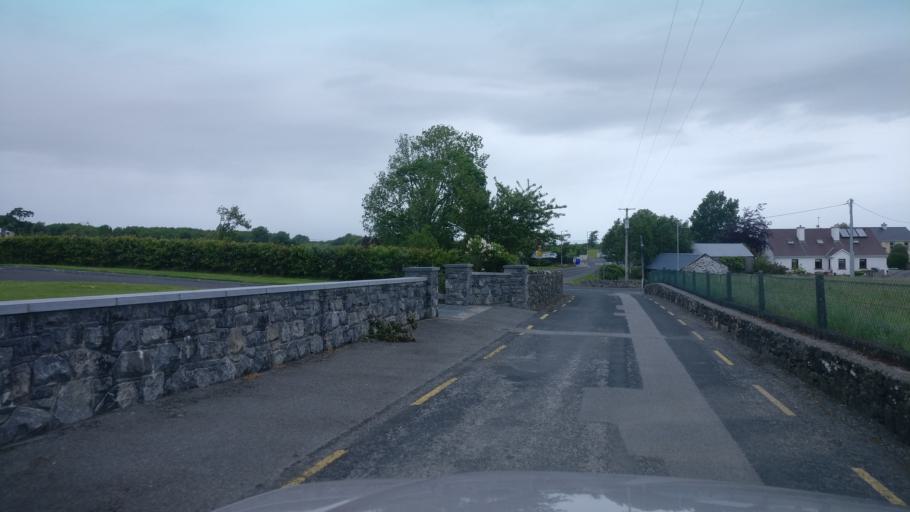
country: IE
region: Connaught
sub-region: County Galway
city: Portumna
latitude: 53.1040
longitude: -8.3942
